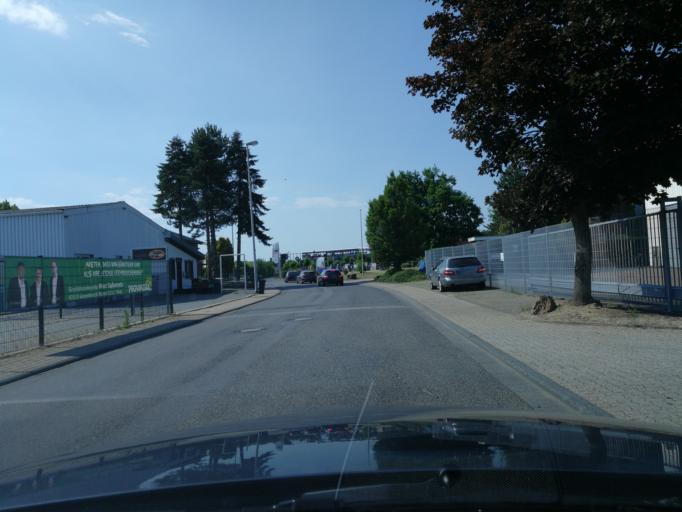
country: DE
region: North Rhine-Westphalia
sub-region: Regierungsbezirk Dusseldorf
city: Grevenbroich
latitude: 51.0896
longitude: 6.6190
